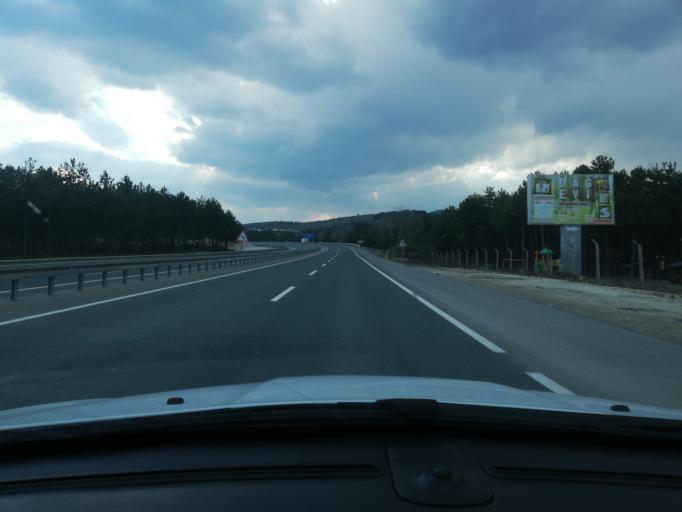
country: TR
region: Kastamonu
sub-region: Cide
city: Kastamonu
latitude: 41.3759
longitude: 33.7362
